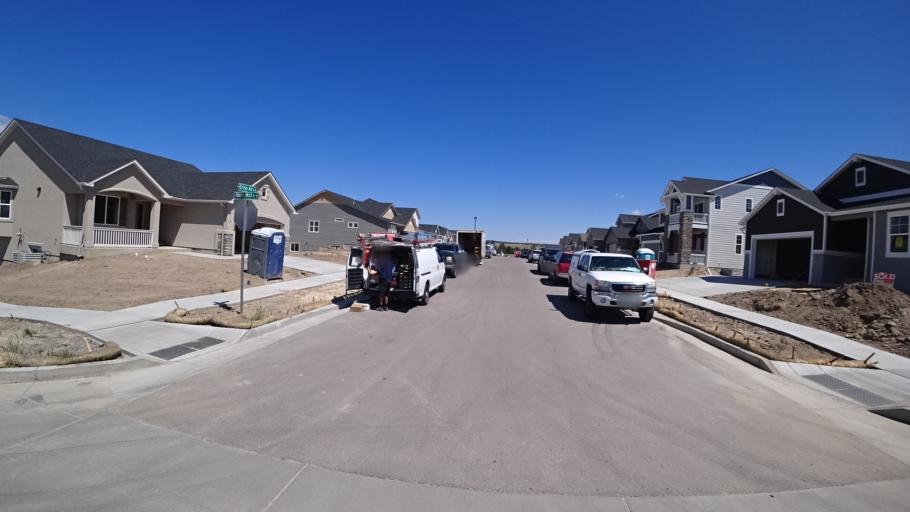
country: US
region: Colorado
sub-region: El Paso County
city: Black Forest
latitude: 38.9928
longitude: -104.7703
